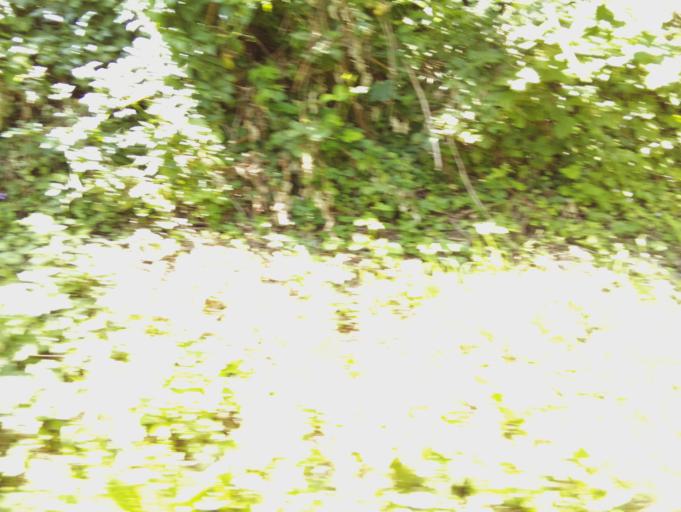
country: CH
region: Zurich
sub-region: Bezirk Andelfingen
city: Grossandelfingen
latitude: 47.5976
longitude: 8.6788
